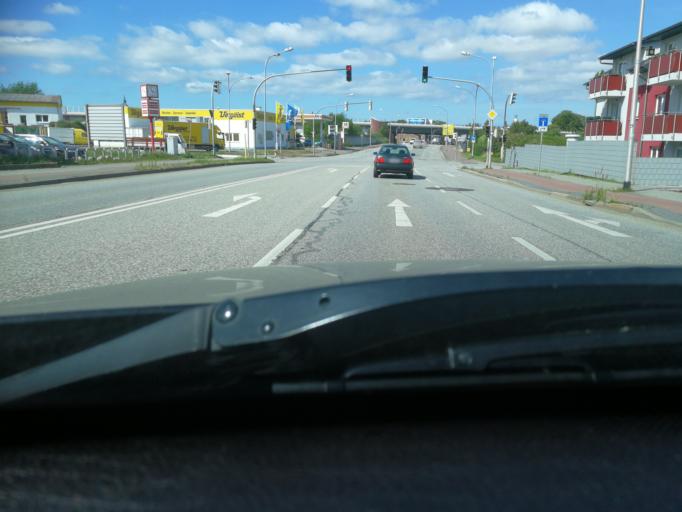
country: DE
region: Mecklenburg-Vorpommern
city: Stralsund
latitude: 54.2972
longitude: 13.0919
